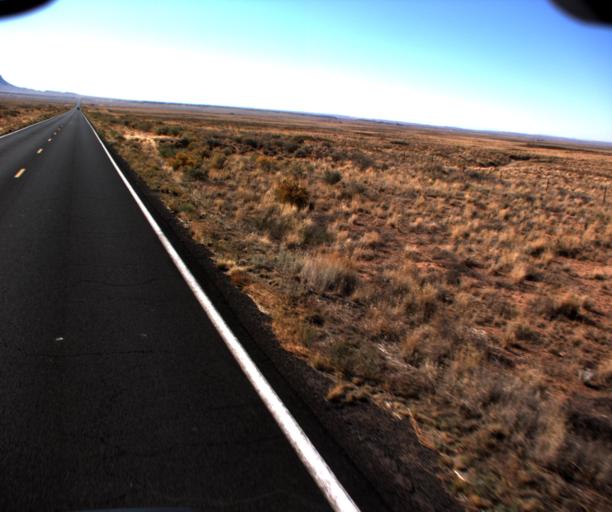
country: US
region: Arizona
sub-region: Navajo County
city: Dilkon
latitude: 35.3889
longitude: -110.4257
